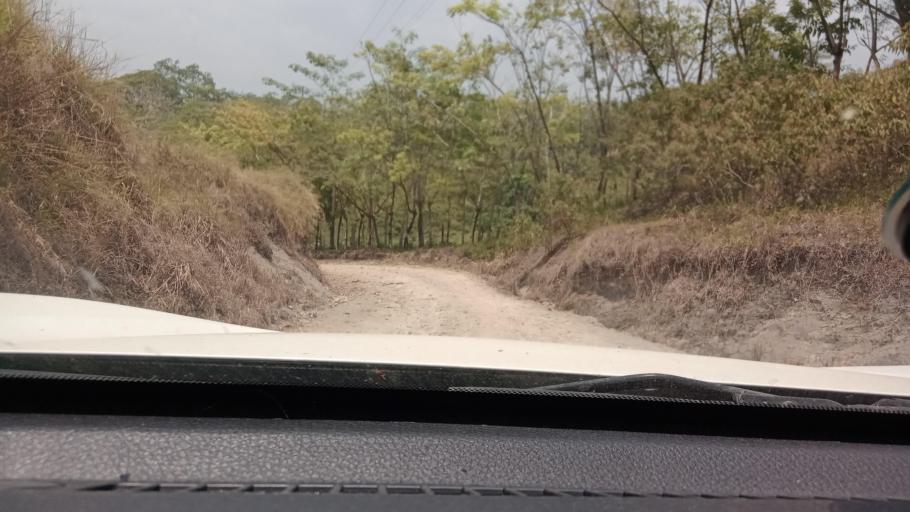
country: MX
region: Tabasco
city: Chontalpa
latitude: 17.5627
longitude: -93.7160
